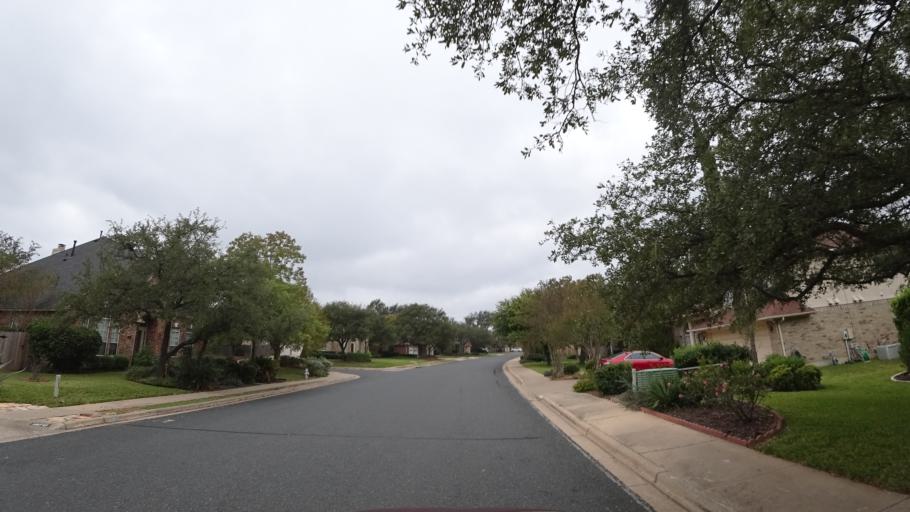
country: US
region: Texas
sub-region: Williamson County
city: Anderson Mill
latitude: 30.4369
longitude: -97.8201
